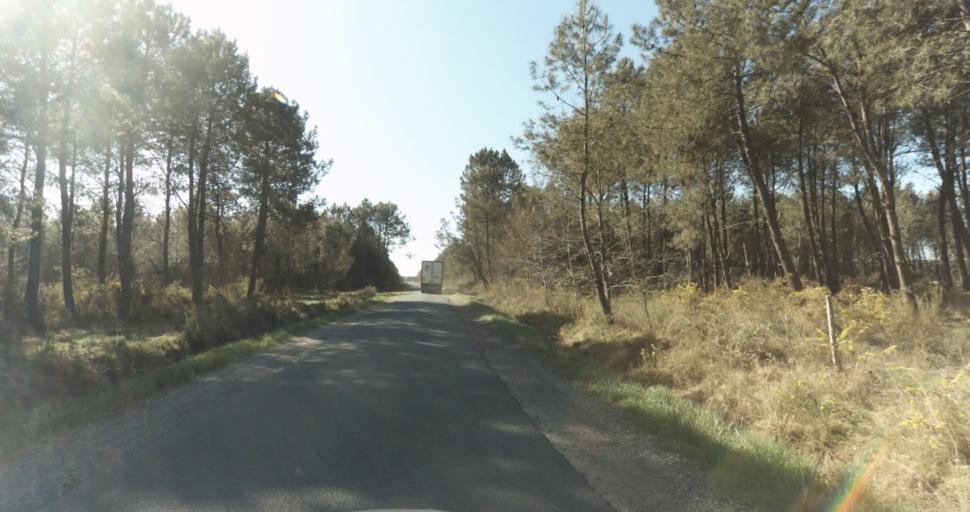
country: FR
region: Aquitaine
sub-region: Departement de la Gironde
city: Marcheprime
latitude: 44.7570
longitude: -0.8509
